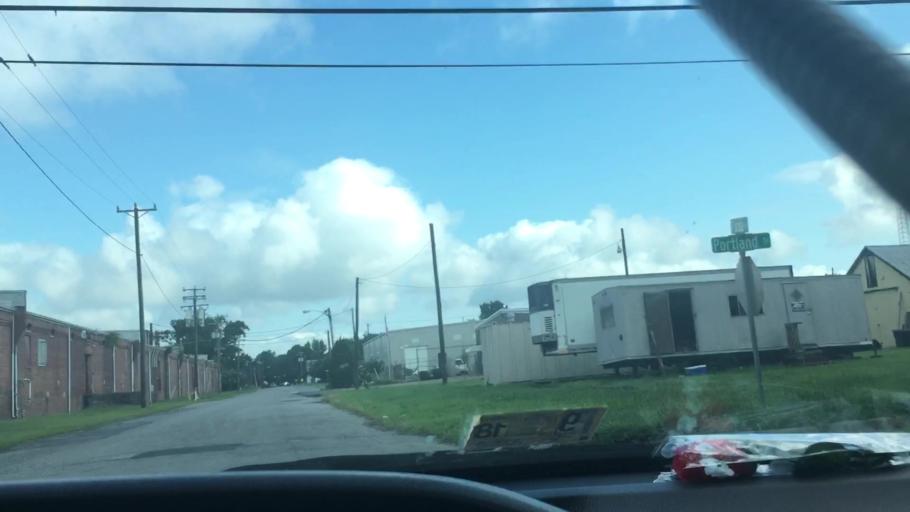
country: US
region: Virginia
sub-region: City of Portsmouth
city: Portsmouth Heights
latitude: 36.8393
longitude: -76.3372
